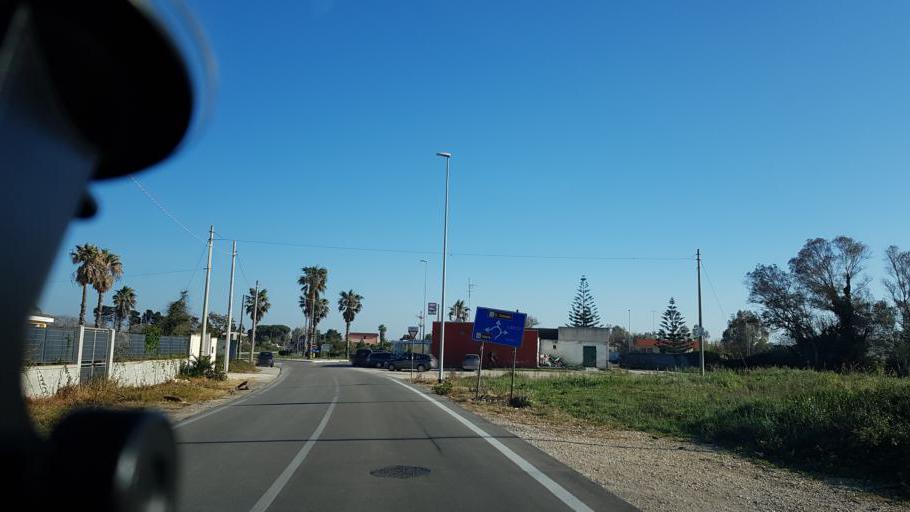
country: IT
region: Apulia
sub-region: Provincia di Lecce
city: Merine
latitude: 40.4282
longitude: 18.2428
